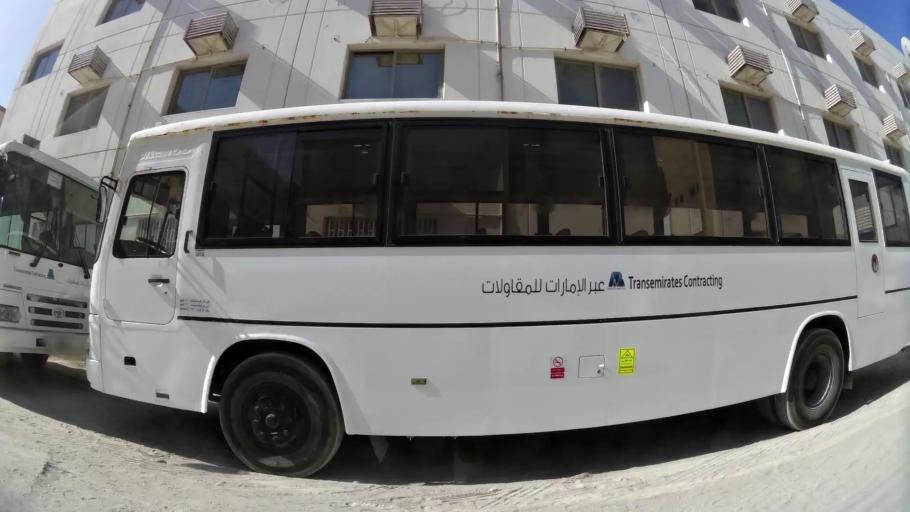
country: AE
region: Dubai
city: Dubai
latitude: 25.0086
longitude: 55.1066
